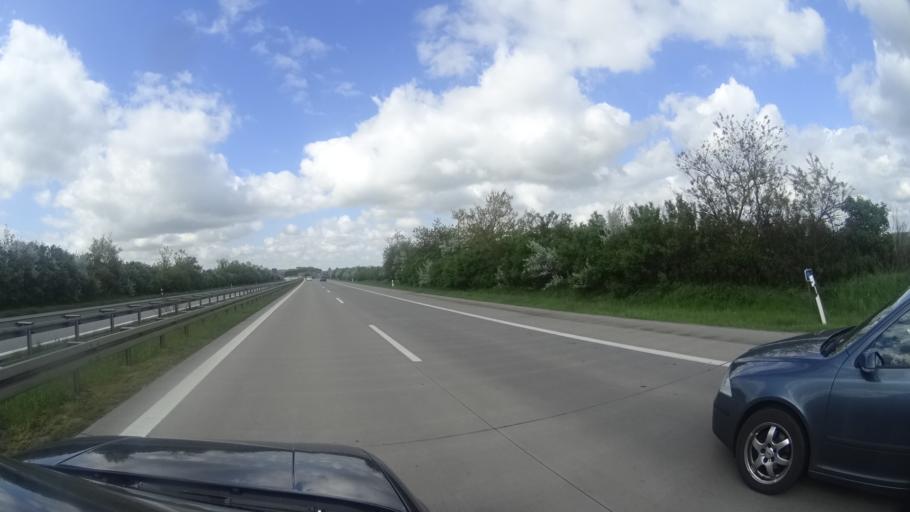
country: DE
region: Mecklenburg-Vorpommern
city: Laage
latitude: 53.8779
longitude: 12.2591
